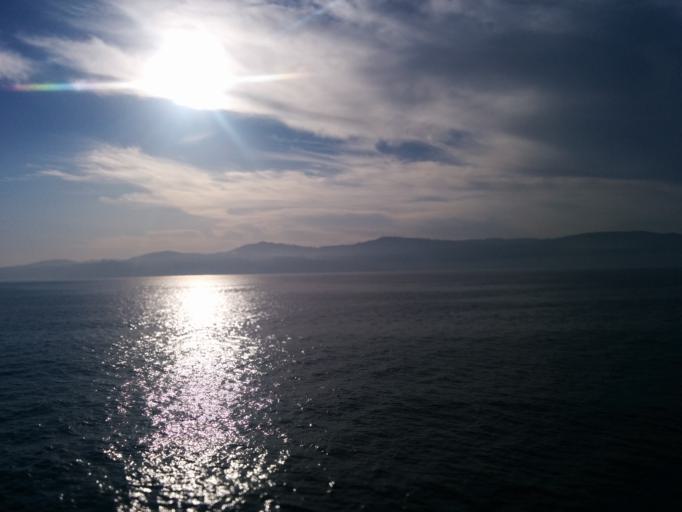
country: MA
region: Tanger-Tetouan
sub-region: Tanger-Assilah
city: Tangier
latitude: 35.8164
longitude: -5.7789
